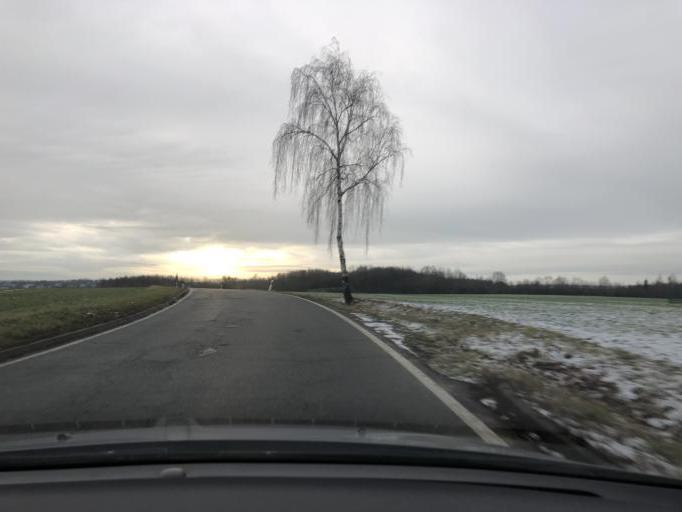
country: DE
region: Saxony
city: Niederfrohna
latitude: 50.8745
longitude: 12.7258
